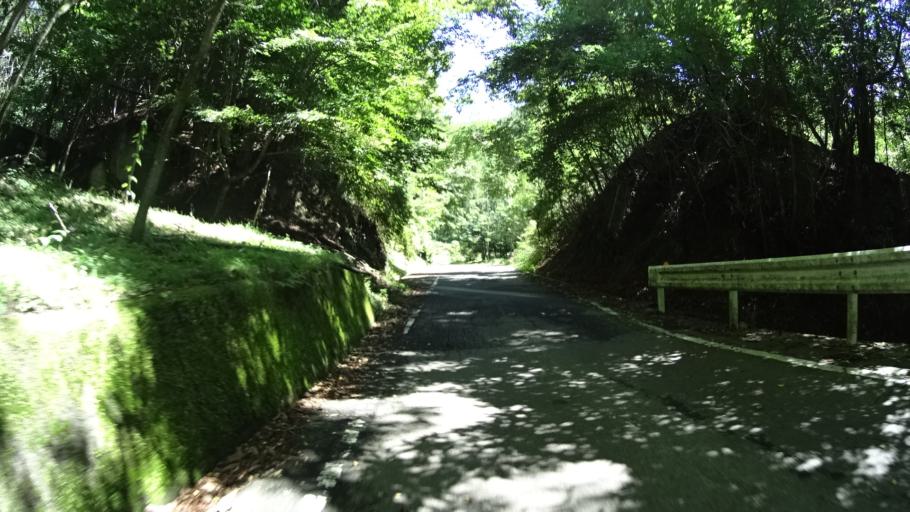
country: JP
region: Yamanashi
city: Enzan
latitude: 35.7435
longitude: 138.8275
